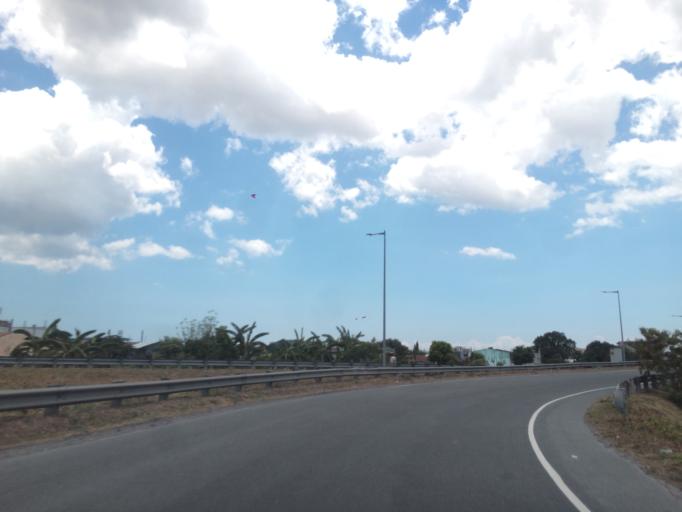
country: PH
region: Calabarzon
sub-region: Province of Rizal
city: Valenzuela
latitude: 14.6922
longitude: 121.0000
